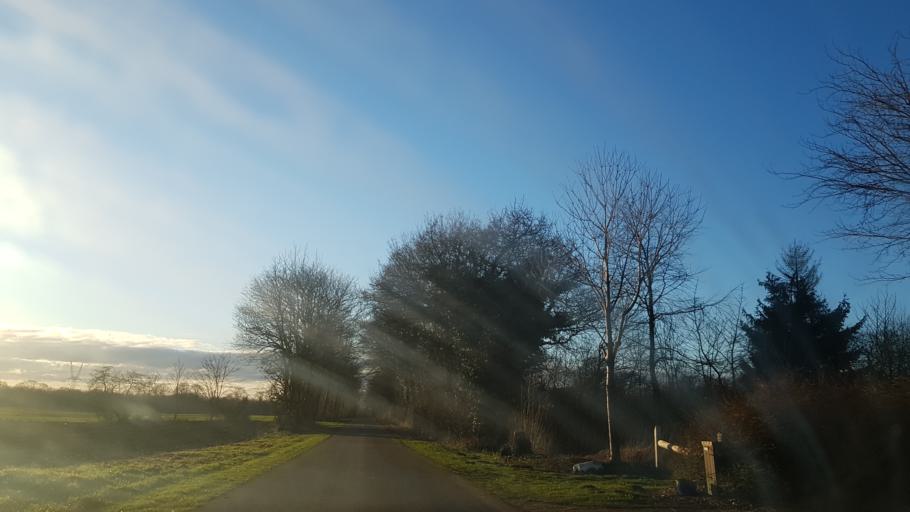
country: DK
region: South Denmark
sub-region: Kolding Kommune
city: Christiansfeld
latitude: 55.4219
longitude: 9.4726
